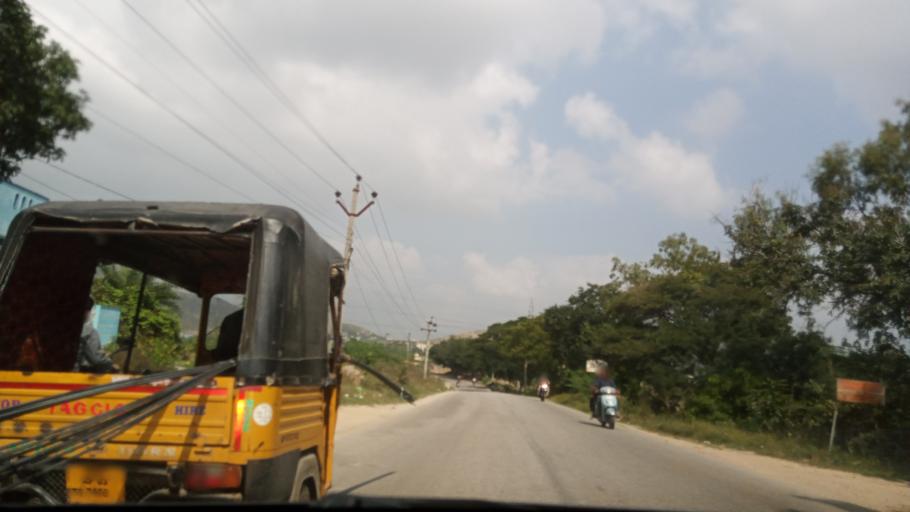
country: IN
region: Andhra Pradesh
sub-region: Chittoor
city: Madanapalle
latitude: 13.5727
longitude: 78.5172
